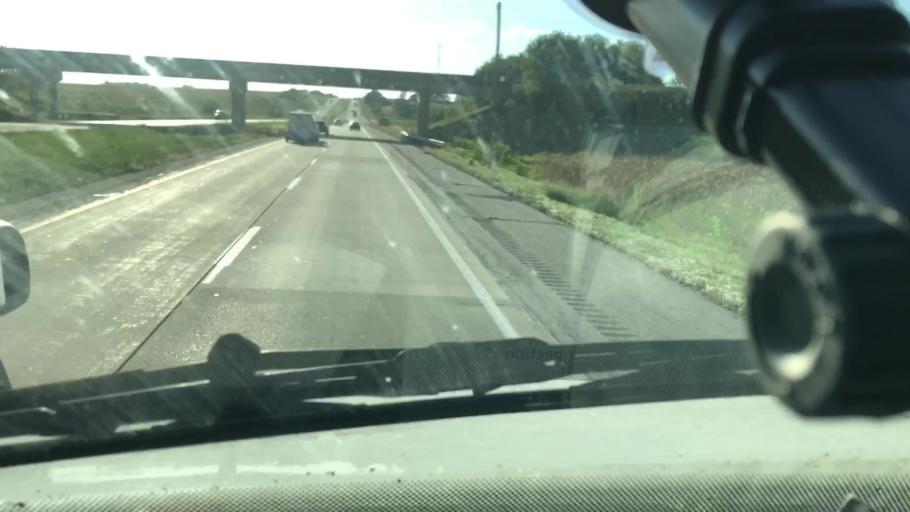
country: US
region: Iowa
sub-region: Pottawattamie County
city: Avoca
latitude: 41.4991
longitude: -95.4502
